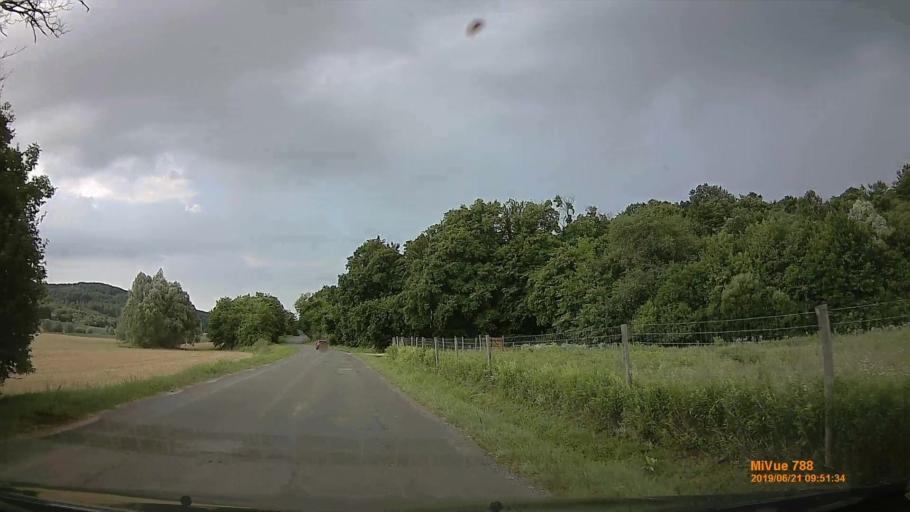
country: HU
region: Baranya
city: Sasd
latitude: 46.2507
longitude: 18.0214
